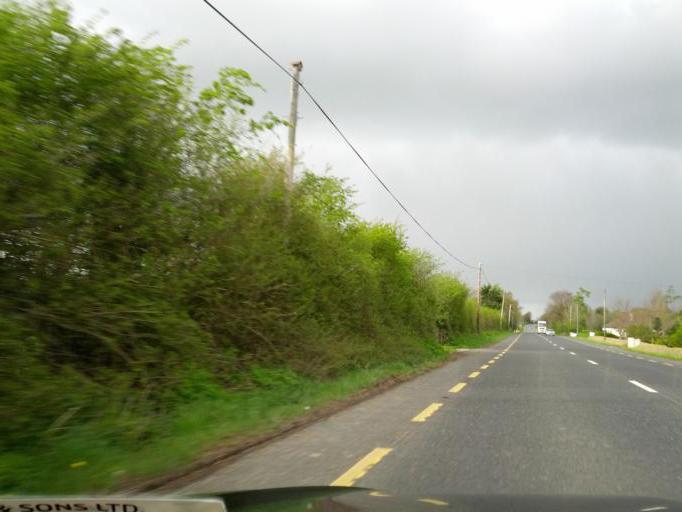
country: IE
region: Leinster
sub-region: An Mhi
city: Dunshaughlin
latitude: 53.5512
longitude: -6.5731
